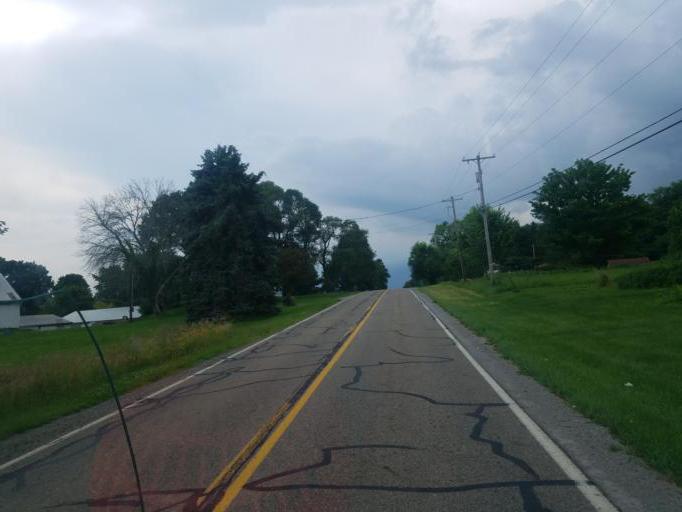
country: US
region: Ohio
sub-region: Stark County
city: Hartville
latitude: 41.0295
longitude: -81.2873
